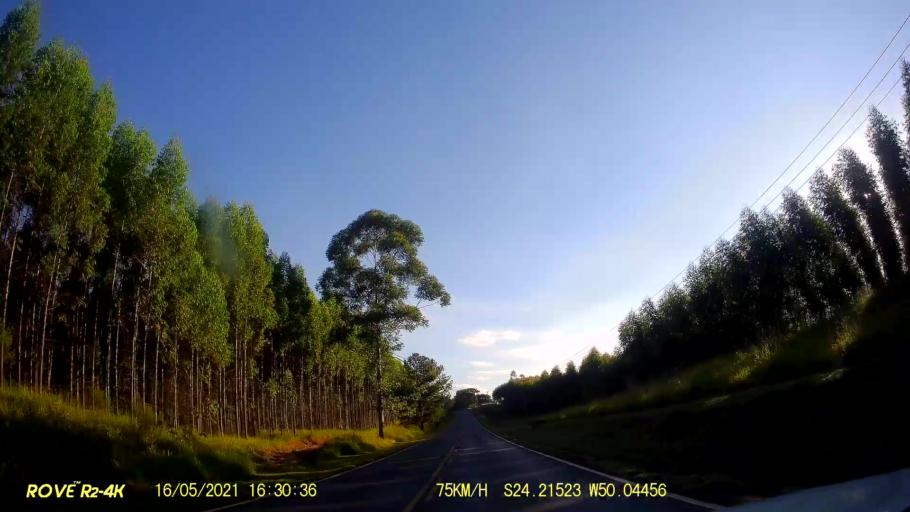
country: BR
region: Parana
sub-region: Pirai Do Sul
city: Pirai do Sul
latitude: -24.2153
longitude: -50.0448
